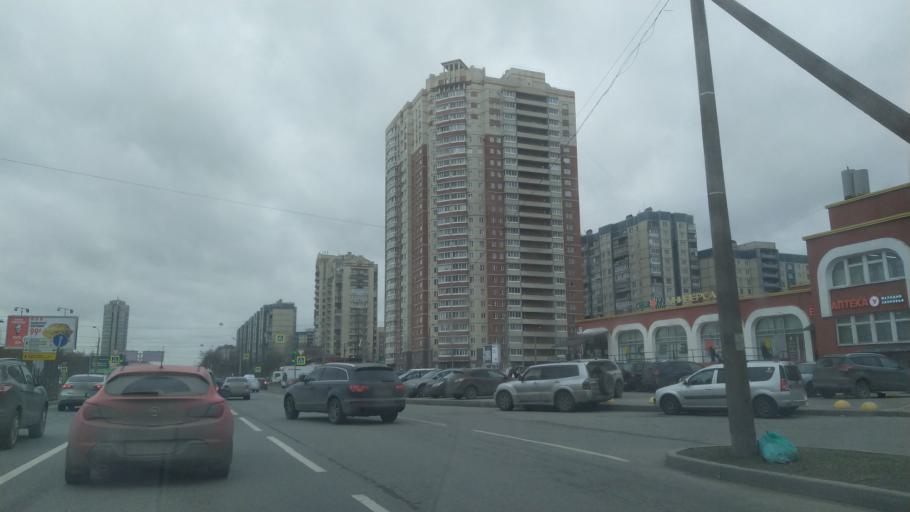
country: RU
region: St.-Petersburg
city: Komendantsky aerodrom
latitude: 60.0129
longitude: 30.2762
